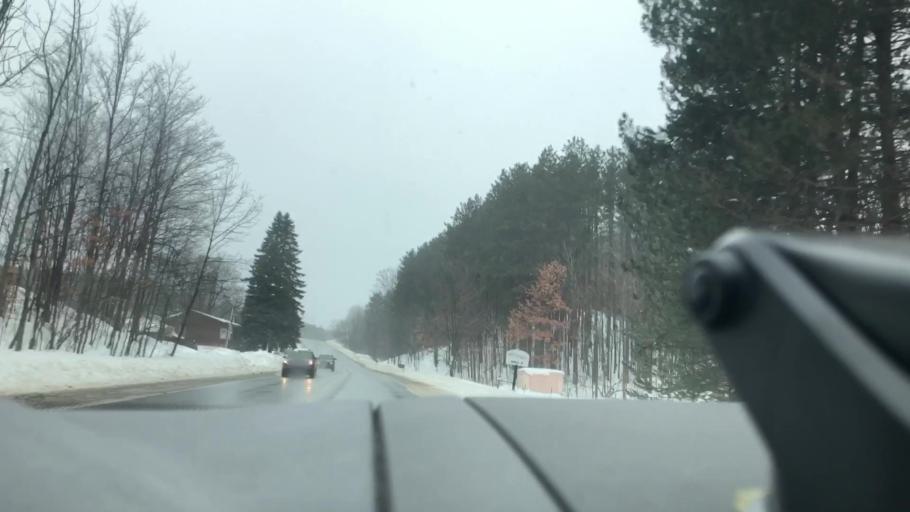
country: US
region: Michigan
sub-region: Charlevoix County
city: East Jordan
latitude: 45.1566
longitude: -85.1559
